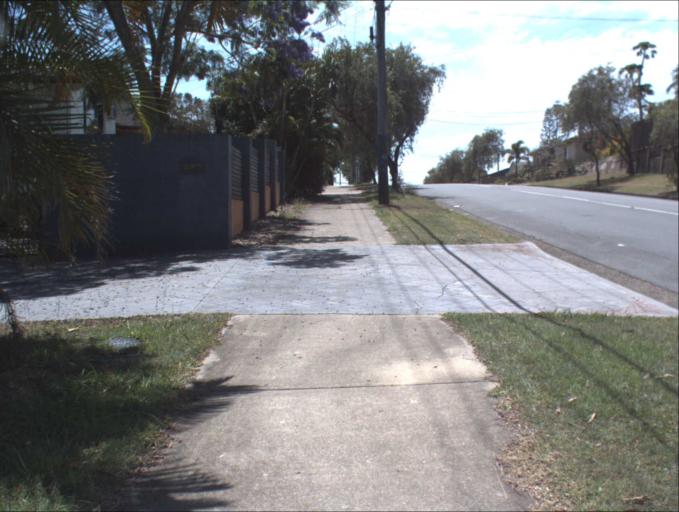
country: AU
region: Queensland
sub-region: Logan
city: Rochedale South
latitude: -27.5933
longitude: 153.1379
